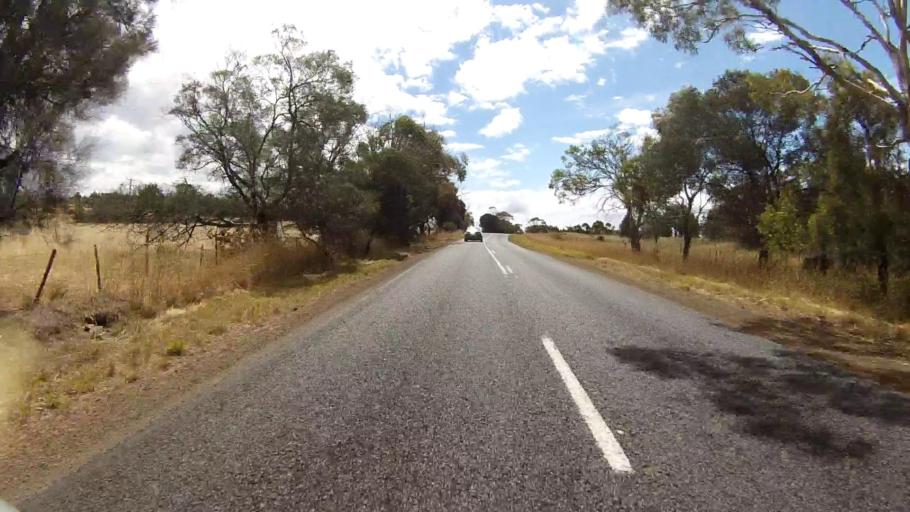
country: AU
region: Tasmania
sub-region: Sorell
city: Sorell
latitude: -42.1608
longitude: 148.0710
